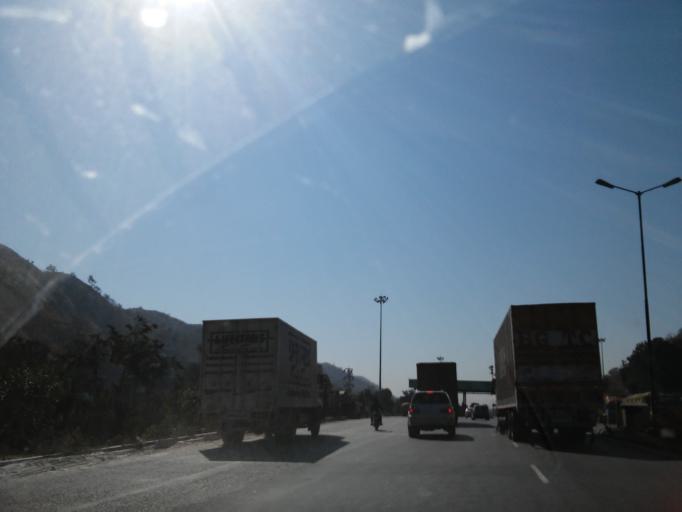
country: IN
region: Rajasthan
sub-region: Udaipur
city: Udaipur
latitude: 24.2731
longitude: 73.6739
